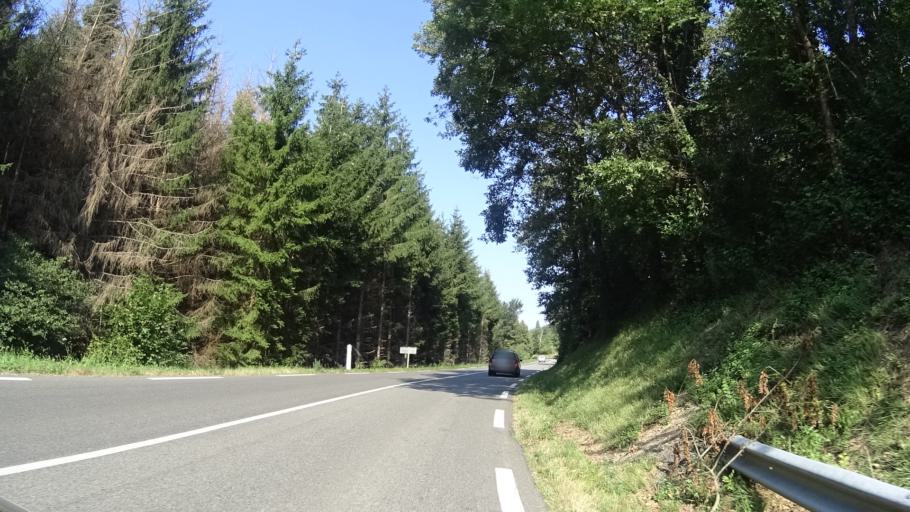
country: FR
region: Midi-Pyrenees
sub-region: Departement de l'Ariege
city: Lavelanet
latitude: 42.9217
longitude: 1.8810
